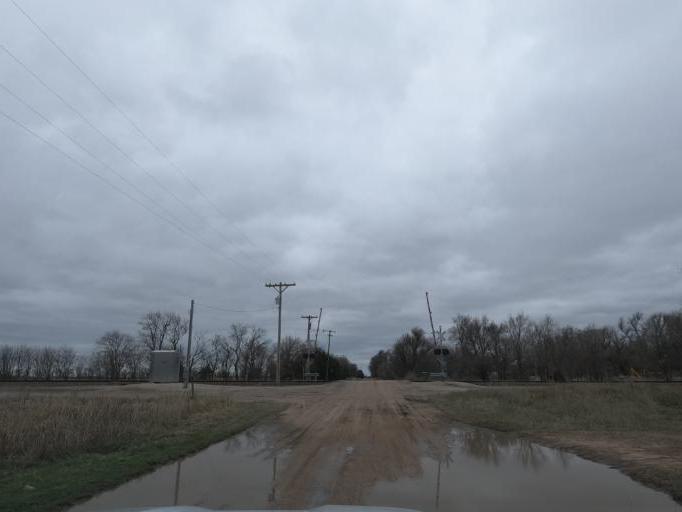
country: US
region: Kansas
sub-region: Rice County
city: Sterling
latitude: 37.9746
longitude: -98.3072
